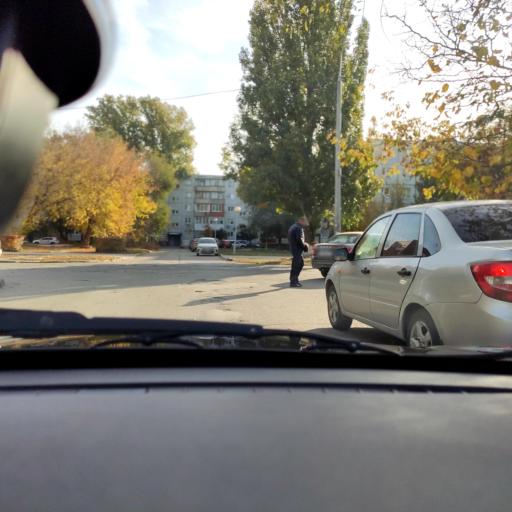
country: RU
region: Samara
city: Tol'yatti
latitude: 53.5322
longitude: 49.2664
